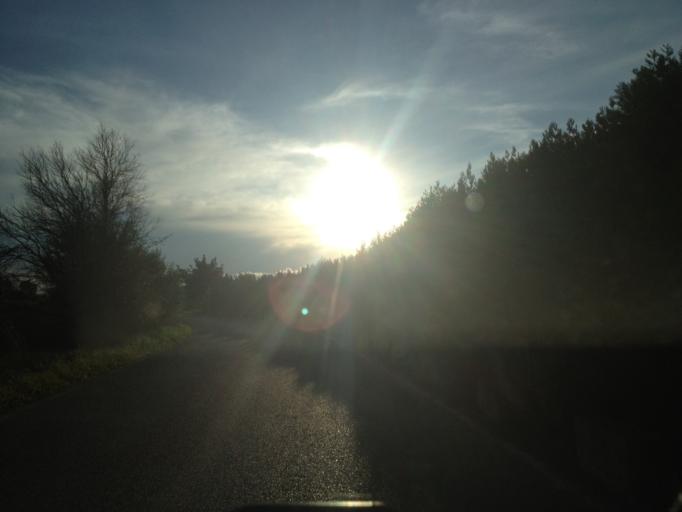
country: ES
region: Balearic Islands
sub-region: Illes Balears
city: Santa Maria del Cami
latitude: 39.6705
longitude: 2.7831
